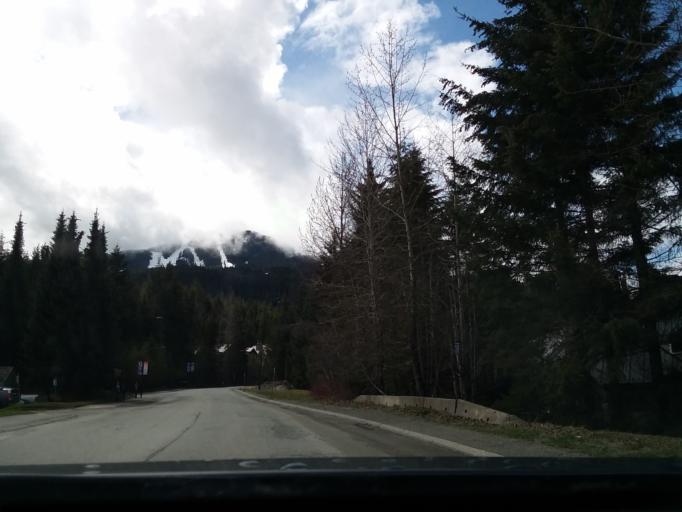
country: CA
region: British Columbia
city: Whistler
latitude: 50.1151
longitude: -122.9494
